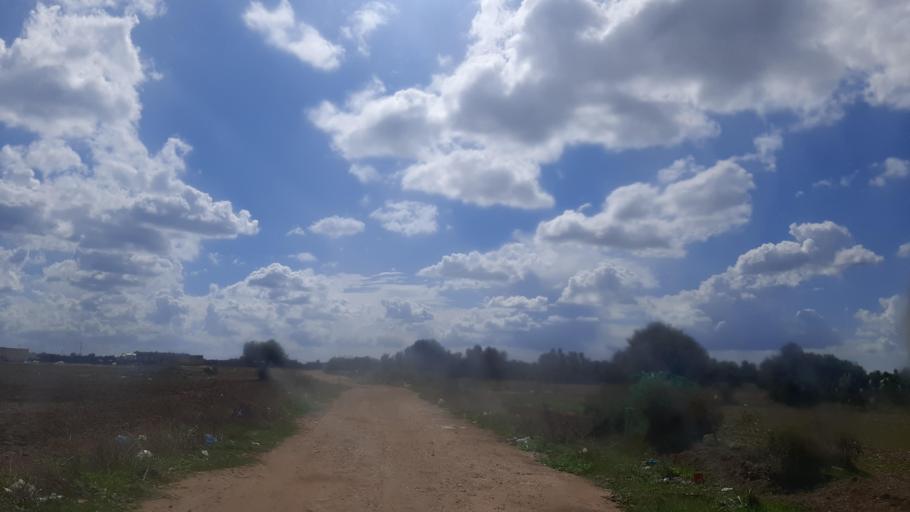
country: TN
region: Nabul
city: Korba
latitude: 36.6002
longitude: 10.8564
